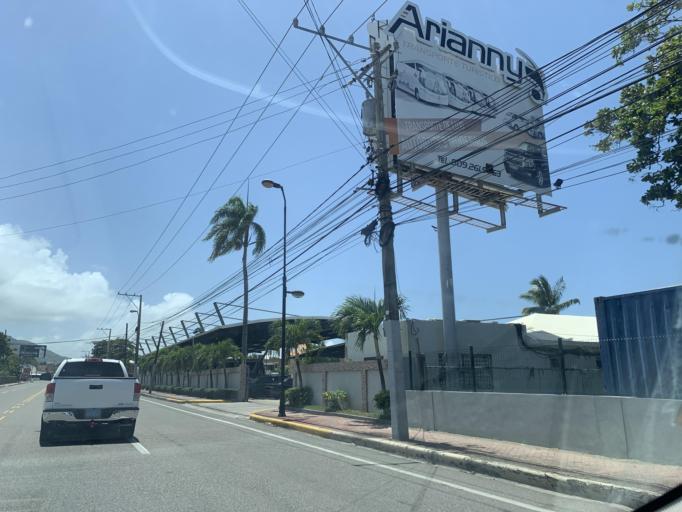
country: DO
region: Puerto Plata
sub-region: Puerto Plata
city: Puerto Plata
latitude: 19.7771
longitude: -70.6633
